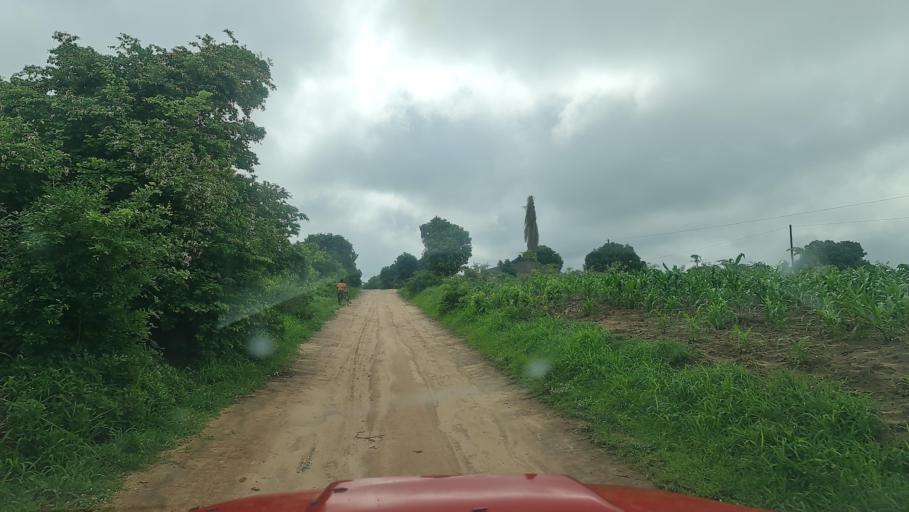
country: MW
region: Southern Region
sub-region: Nsanje District
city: Nsanje
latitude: -17.2029
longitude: 35.6904
